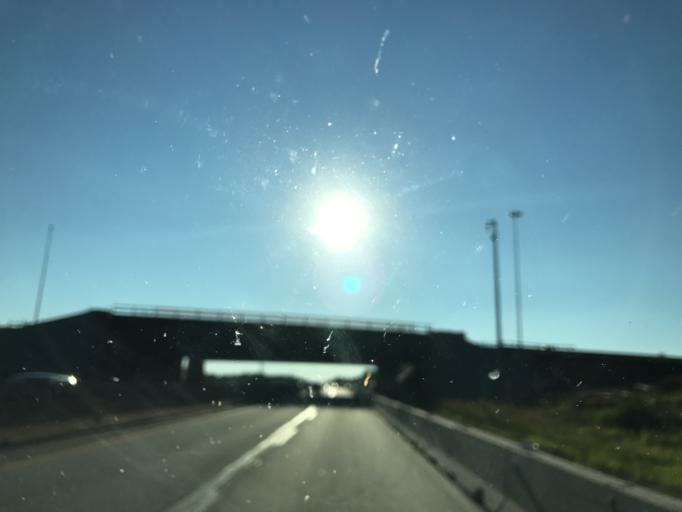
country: US
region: Pennsylvania
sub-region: Bucks County
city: Trevose
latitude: 40.1320
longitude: -74.9704
